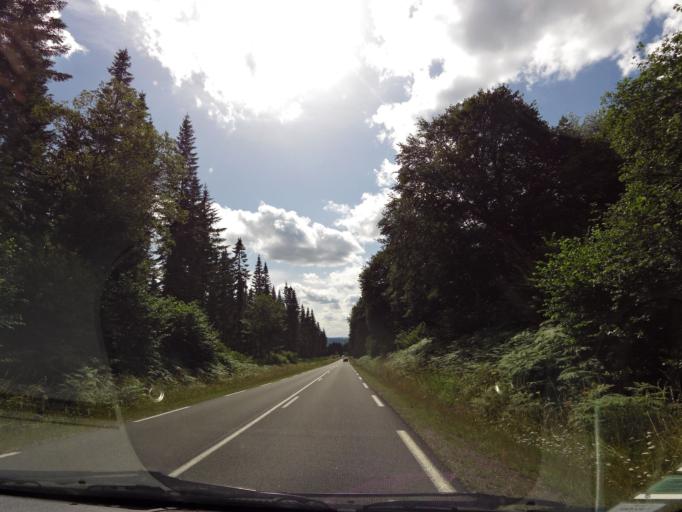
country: FR
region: Auvergne
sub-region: Departement du Puy-de-Dome
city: Saint-Genes-Champanelle
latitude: 45.7388
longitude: 2.9380
